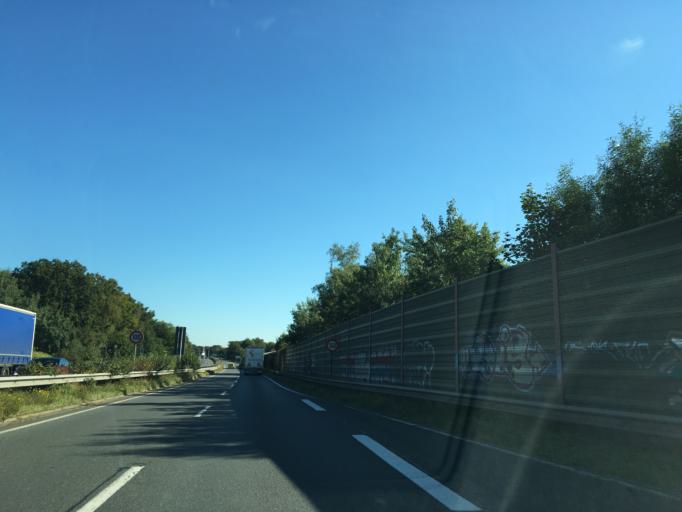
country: DE
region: Lower Saxony
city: Lueneburg
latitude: 53.2755
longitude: 10.4074
